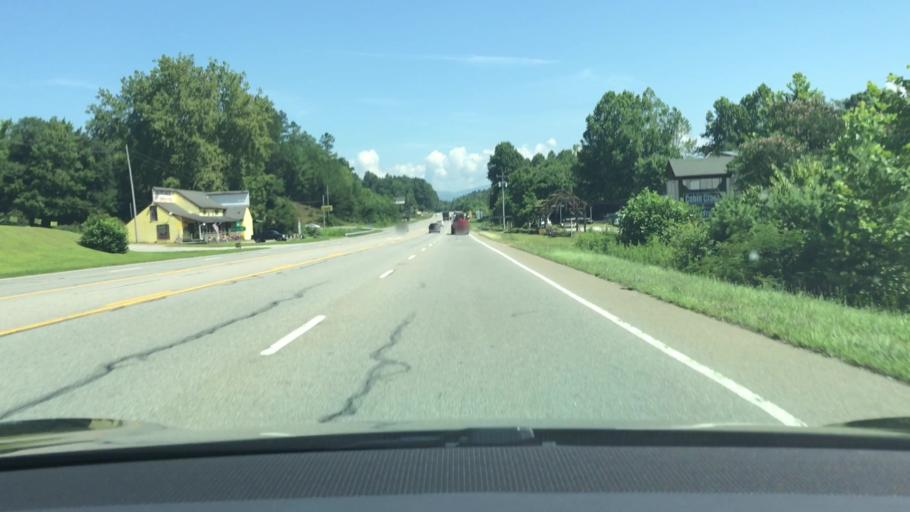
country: US
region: North Carolina
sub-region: Macon County
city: Franklin
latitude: 35.0819
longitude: -83.3844
